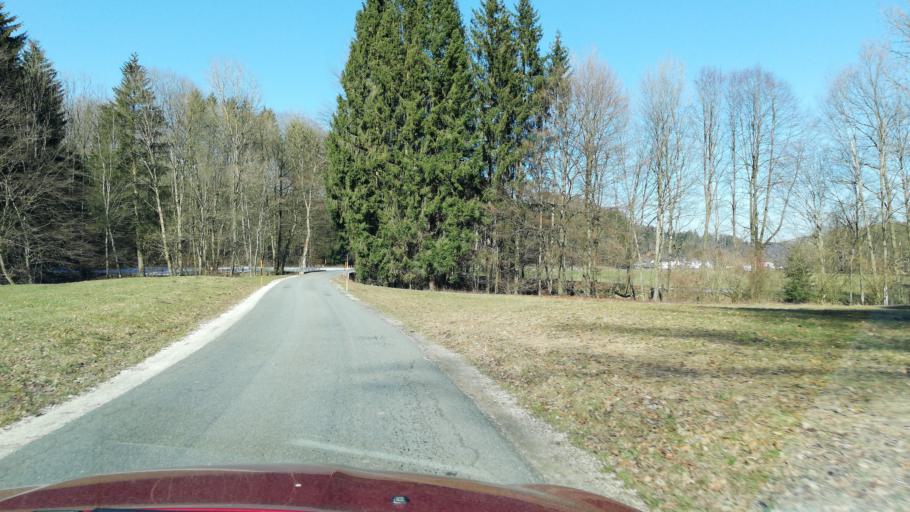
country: AT
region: Upper Austria
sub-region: Politischer Bezirk Vocklabruck
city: Aurach am Hongar
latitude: 47.9729
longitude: 13.7000
